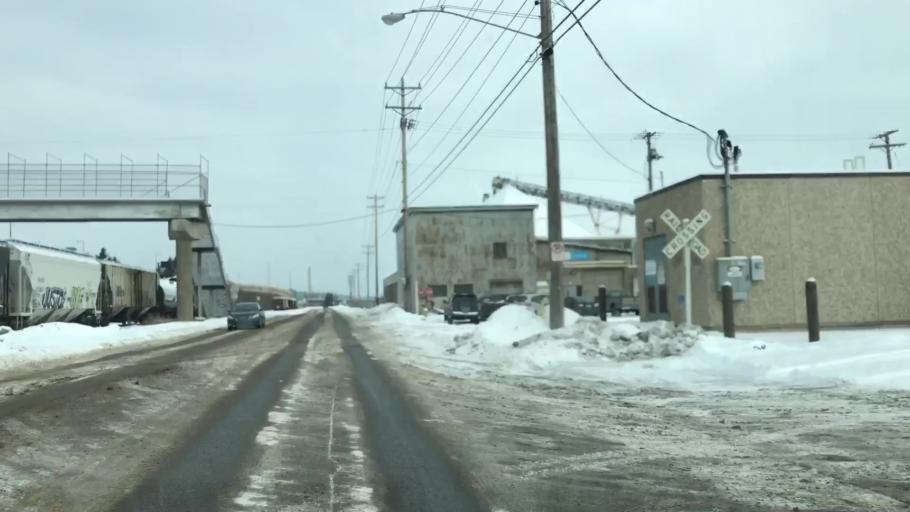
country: US
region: Minnesota
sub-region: Saint Louis County
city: Duluth
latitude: 46.7747
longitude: -92.1099
